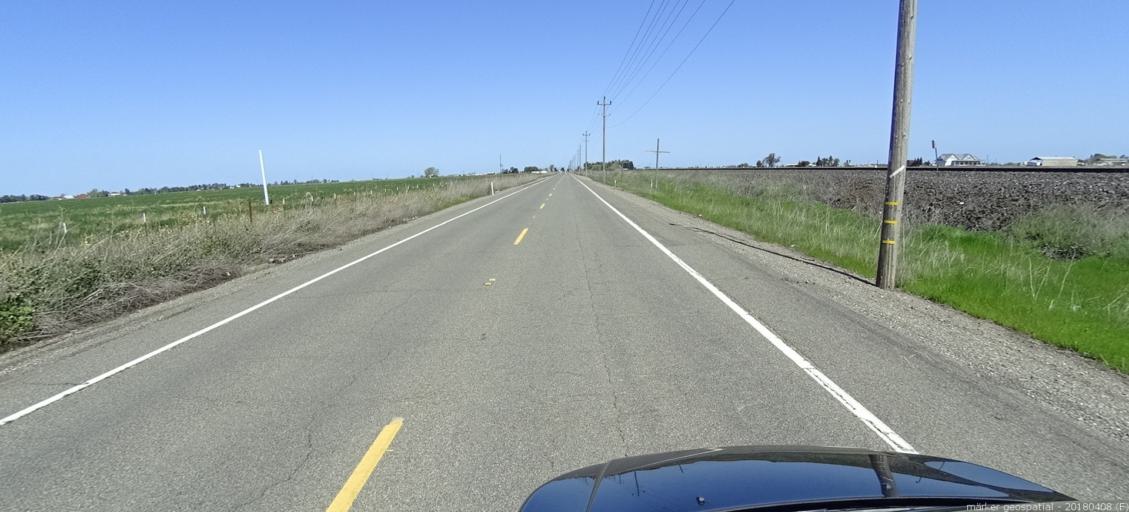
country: US
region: California
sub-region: San Joaquin County
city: Thornton
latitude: 38.3136
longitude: -121.4438
